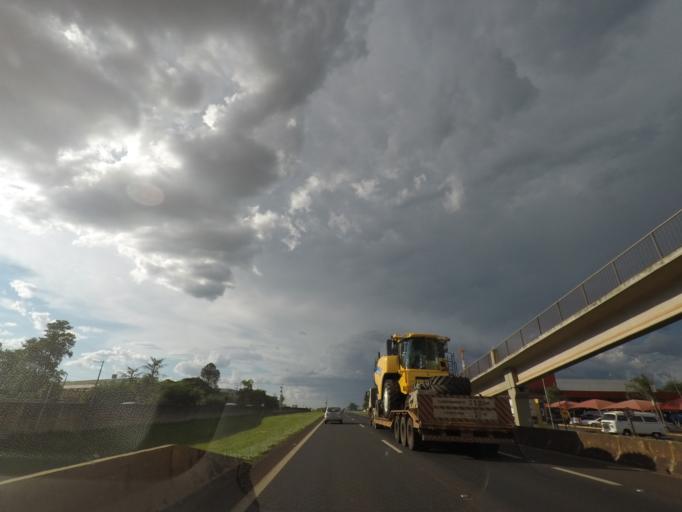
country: BR
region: Sao Paulo
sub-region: Ribeirao Preto
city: Ribeirao Preto
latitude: -21.1023
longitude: -47.7876
